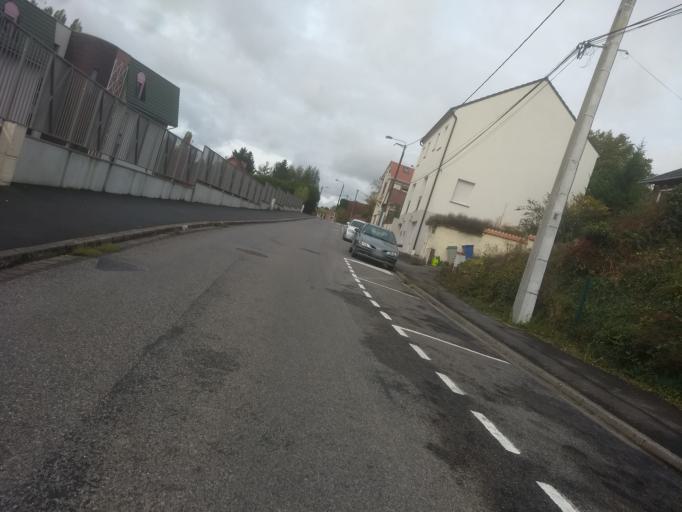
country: FR
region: Nord-Pas-de-Calais
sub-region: Departement du Pas-de-Calais
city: Anzin-Saint-Aubin
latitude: 50.3114
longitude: 2.7464
